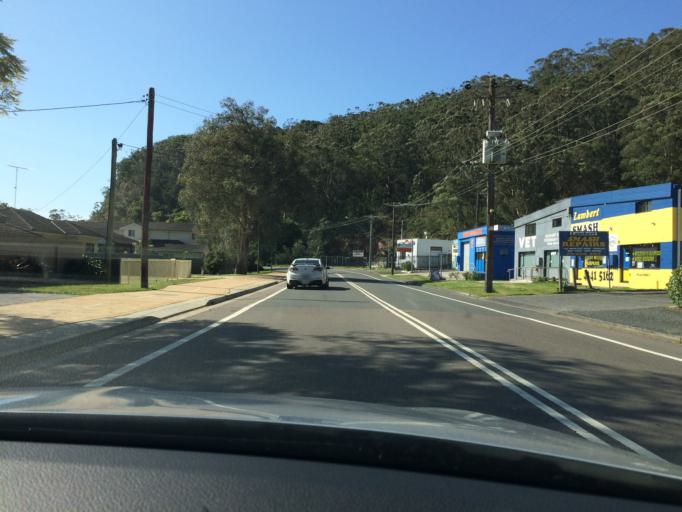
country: AU
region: New South Wales
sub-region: Gosford Shire
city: Ettalong Beach
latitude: -33.5065
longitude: 151.3313
